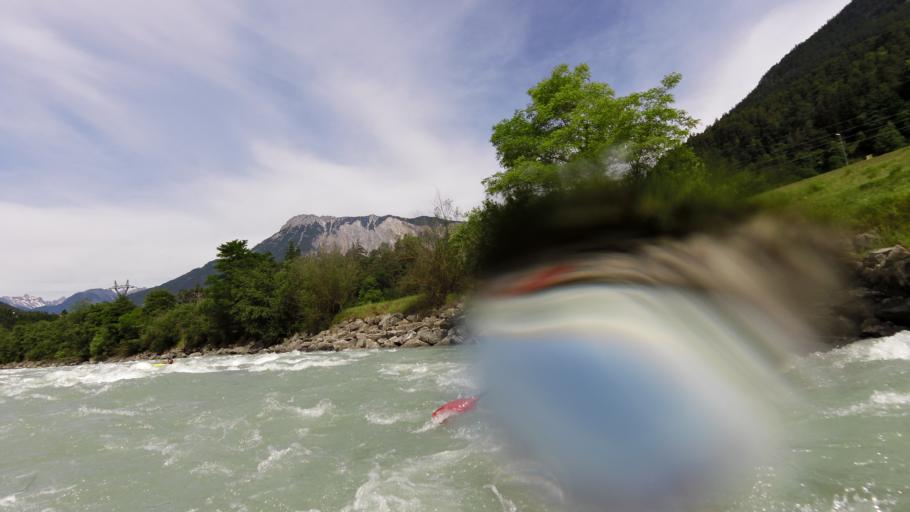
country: AT
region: Tyrol
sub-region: Politischer Bezirk Imst
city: Sautens
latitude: 47.2127
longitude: 10.8693
